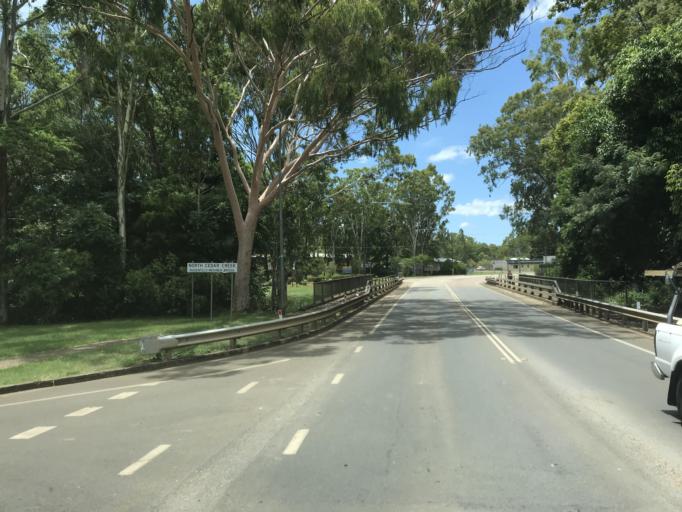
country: AU
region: Queensland
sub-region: Tablelands
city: Ravenshoe
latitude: -17.6096
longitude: 145.4848
